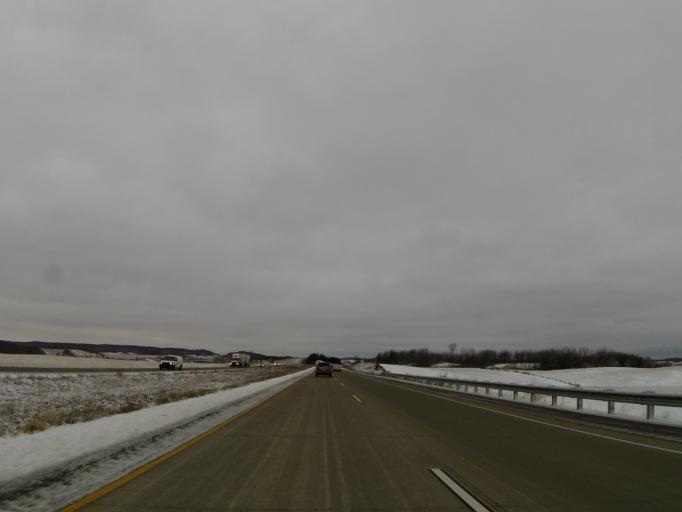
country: US
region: Wisconsin
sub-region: Trempealeau County
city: Osseo
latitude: 44.6333
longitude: -91.2936
